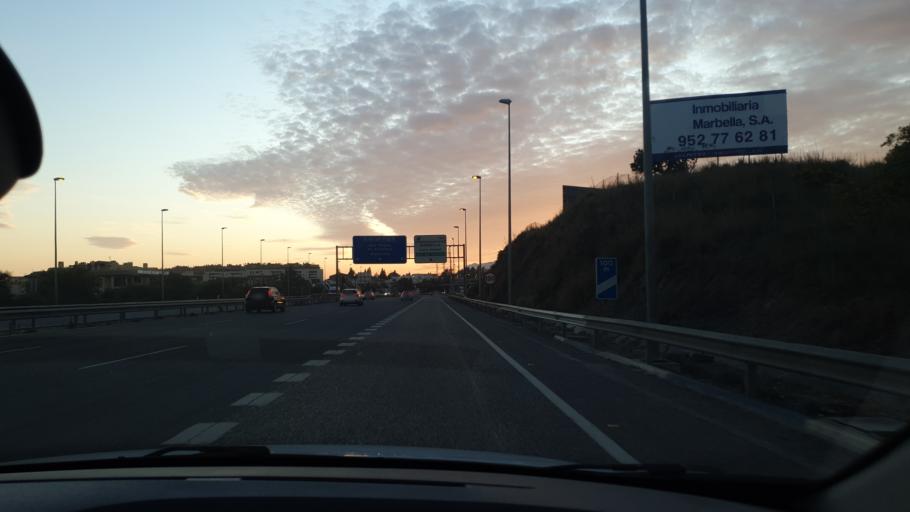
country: ES
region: Andalusia
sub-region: Provincia de Malaga
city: Marbella
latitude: 36.5202
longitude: -4.8847
